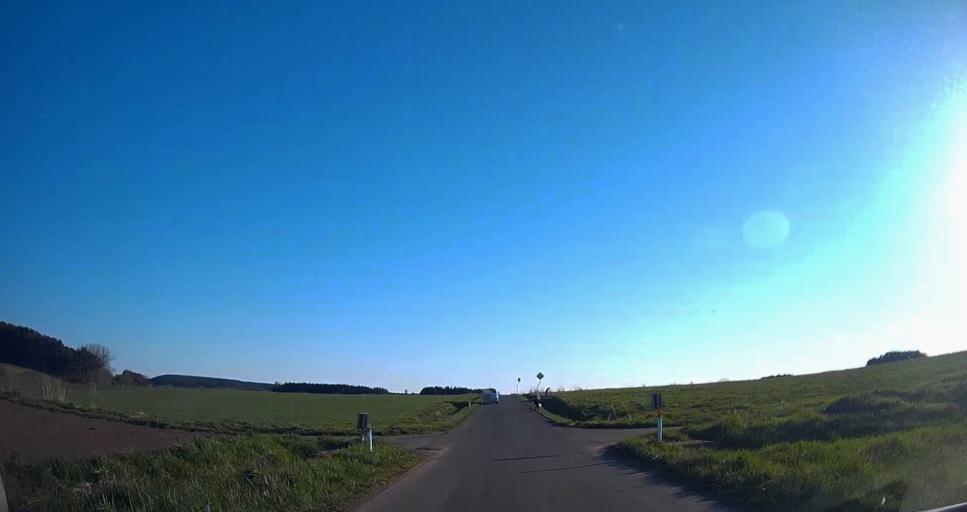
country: JP
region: Aomori
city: Mutsu
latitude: 41.1178
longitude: 141.2762
